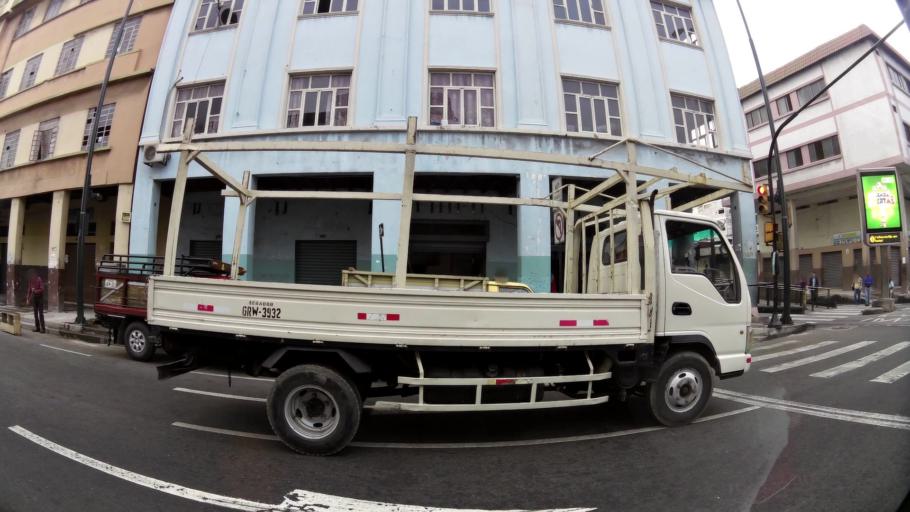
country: EC
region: Guayas
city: Guayaquil
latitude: -2.1941
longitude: -79.8914
